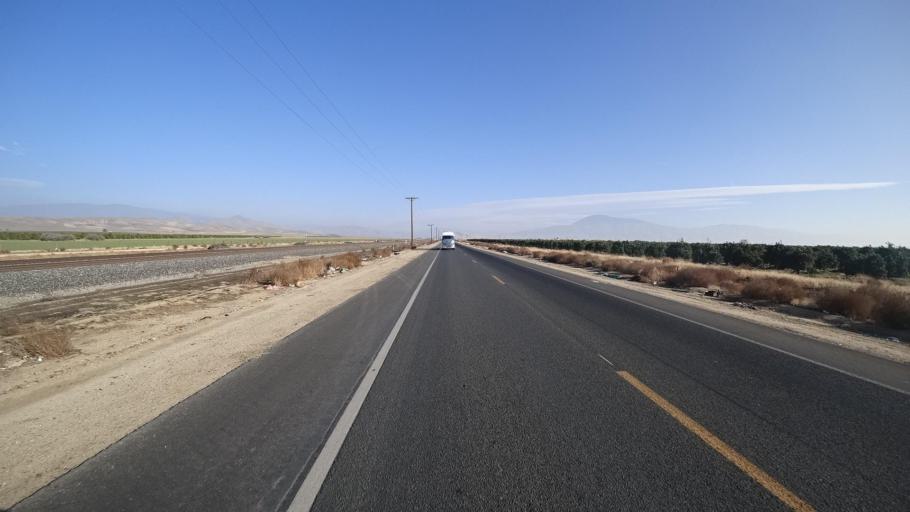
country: US
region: California
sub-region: Kern County
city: Lamont
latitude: 35.3388
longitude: -118.8328
